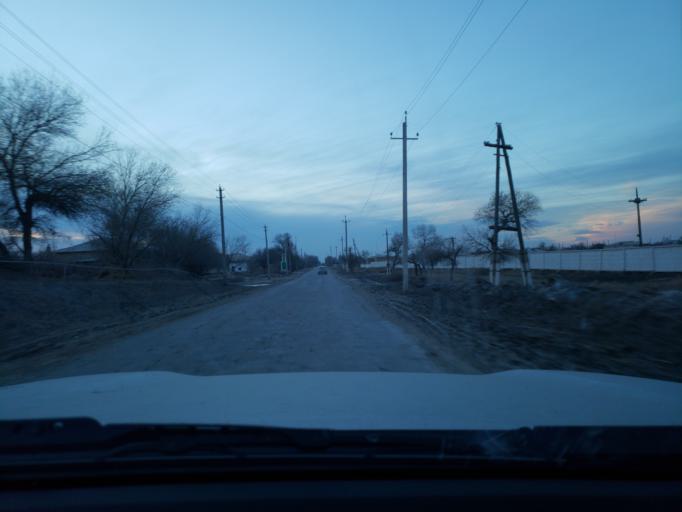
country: TM
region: Dasoguz
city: Tagta
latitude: 41.5838
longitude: 60.0644
